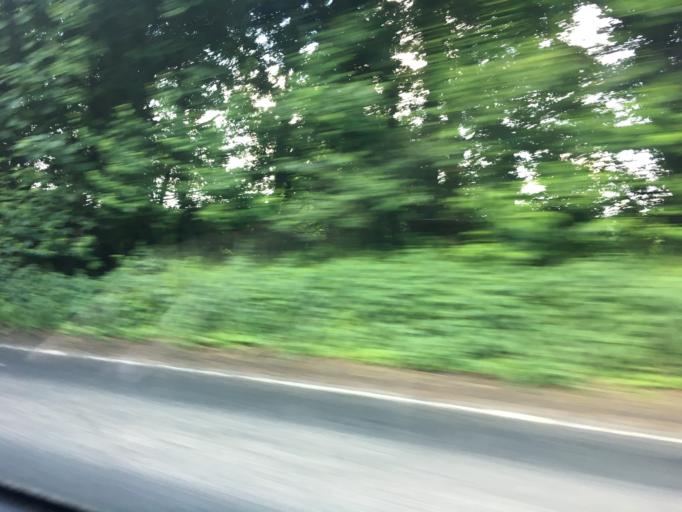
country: GB
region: England
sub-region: Leicestershire
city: Oadby
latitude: 52.6110
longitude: -1.0659
